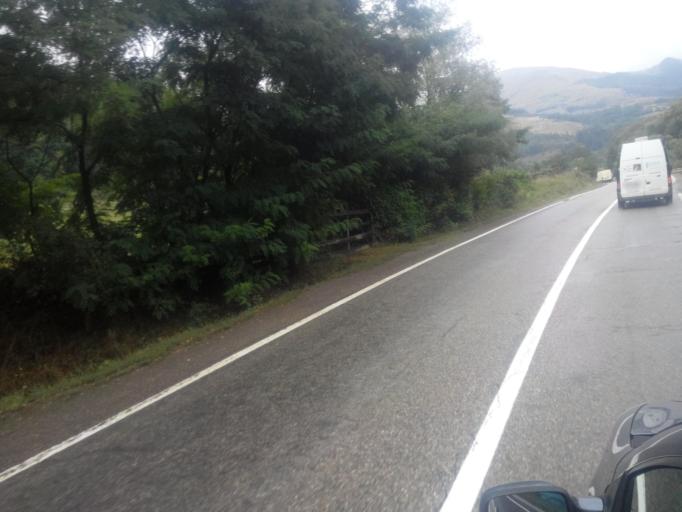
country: RO
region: Alba
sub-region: Comuna Ocolis
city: Ocolis
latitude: 46.4610
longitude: 23.4721
